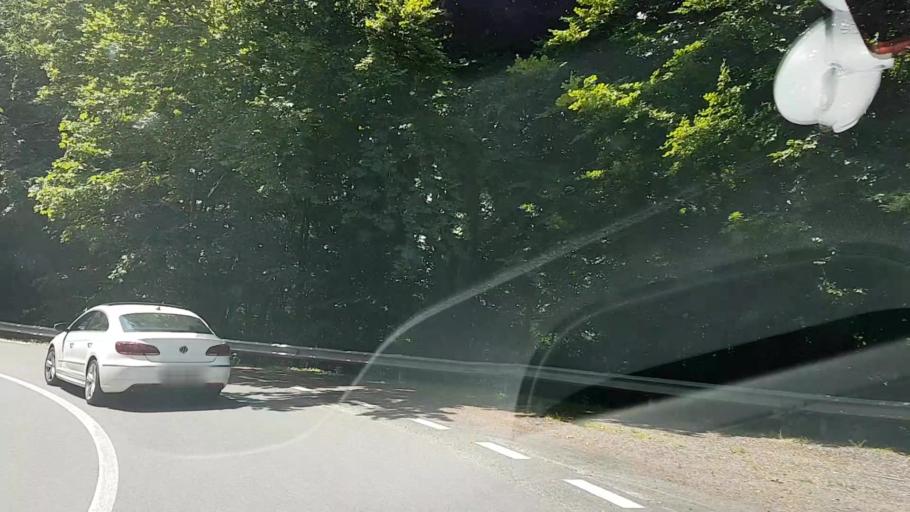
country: RO
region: Sibiu
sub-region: Comuna Cartisoara
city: Cartisoara
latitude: 45.6730
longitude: 24.5879
